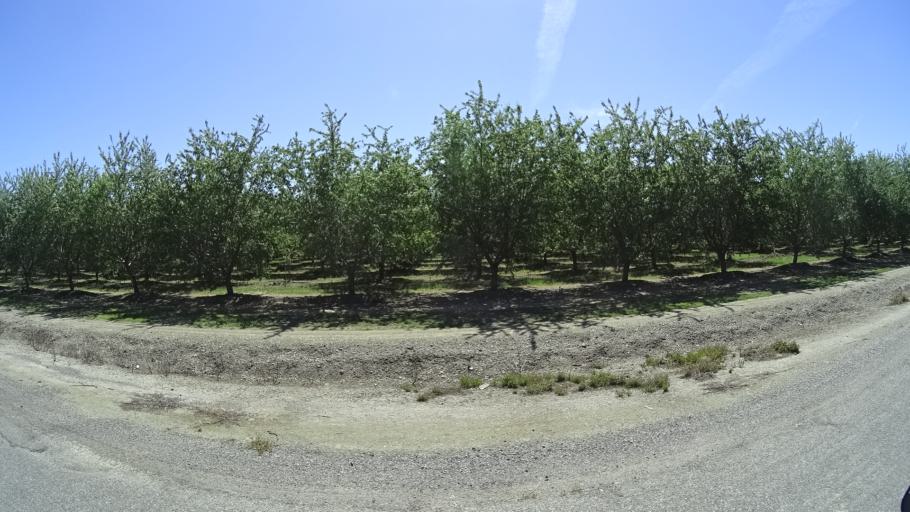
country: US
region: California
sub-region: Glenn County
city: Hamilton City
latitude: 39.7214
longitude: -122.0954
